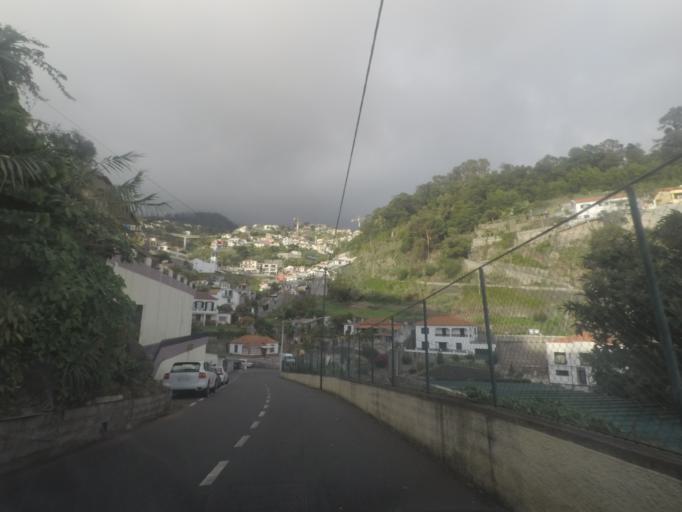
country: PT
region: Madeira
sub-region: Funchal
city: Nossa Senhora do Monte
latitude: 32.6726
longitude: -16.9410
